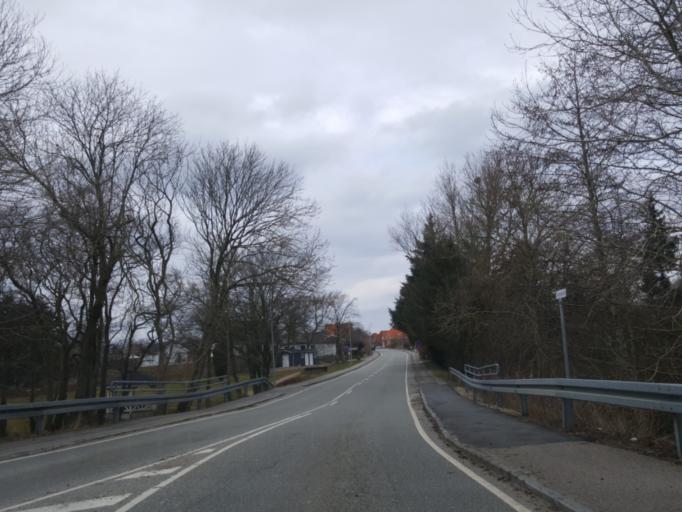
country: DK
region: Central Jutland
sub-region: Lemvig Kommune
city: Lemvig
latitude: 56.4319
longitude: 8.2094
